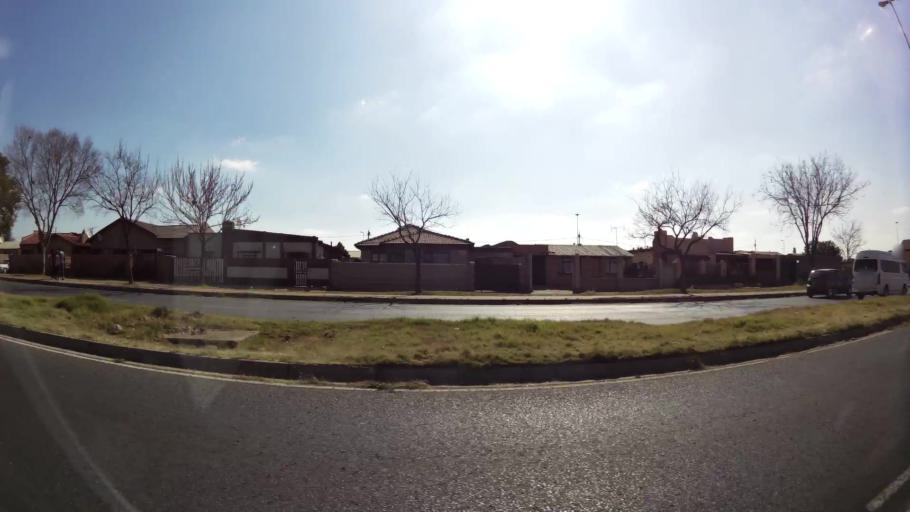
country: ZA
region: Gauteng
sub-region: City of Johannesburg Metropolitan Municipality
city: Soweto
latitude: -26.2773
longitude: 27.8664
